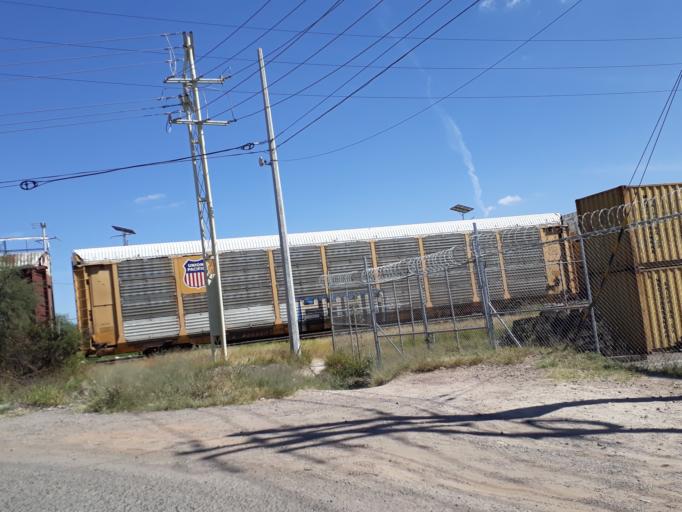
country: MX
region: Aguascalientes
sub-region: Aguascalientes
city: San Sebastian [Fraccionamiento]
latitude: 21.7984
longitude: -102.2769
